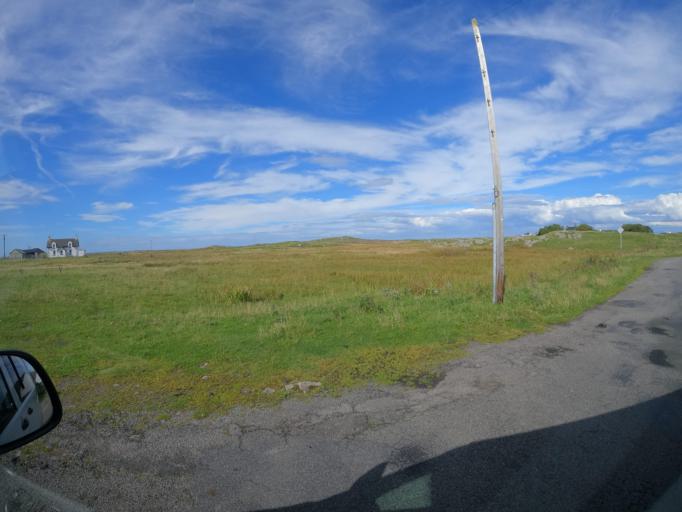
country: GB
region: Scotland
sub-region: Eilean Siar
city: Barra
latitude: 56.4967
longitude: -6.8115
